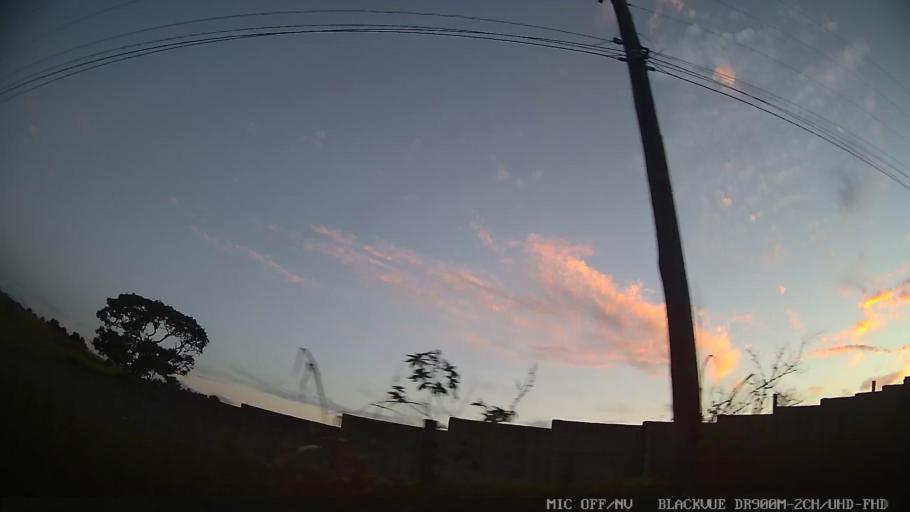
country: BR
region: Sao Paulo
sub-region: Itupeva
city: Itupeva
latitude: -23.1660
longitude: -47.1383
